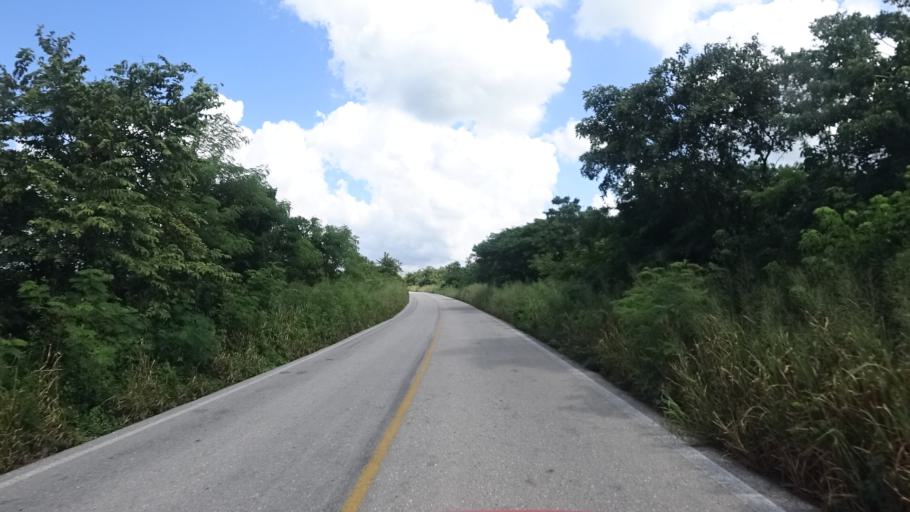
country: MX
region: Yucatan
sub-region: Panaba
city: Loche
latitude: 21.4532
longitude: -88.1327
